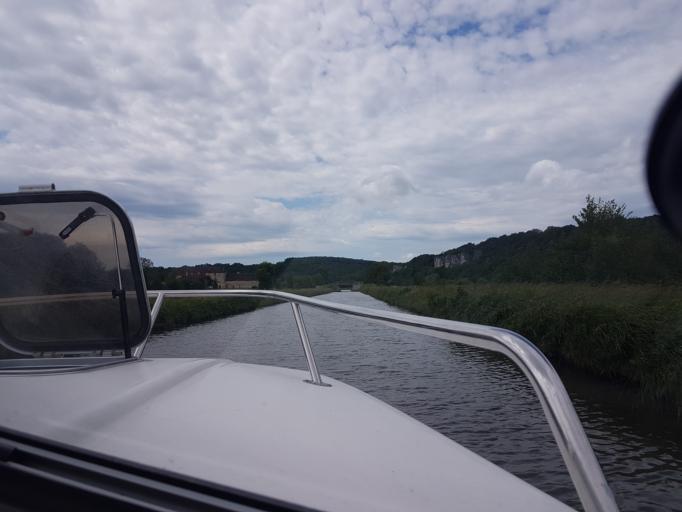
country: FR
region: Bourgogne
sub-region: Departement de la Nievre
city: Clamecy
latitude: 47.5004
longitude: 3.5171
